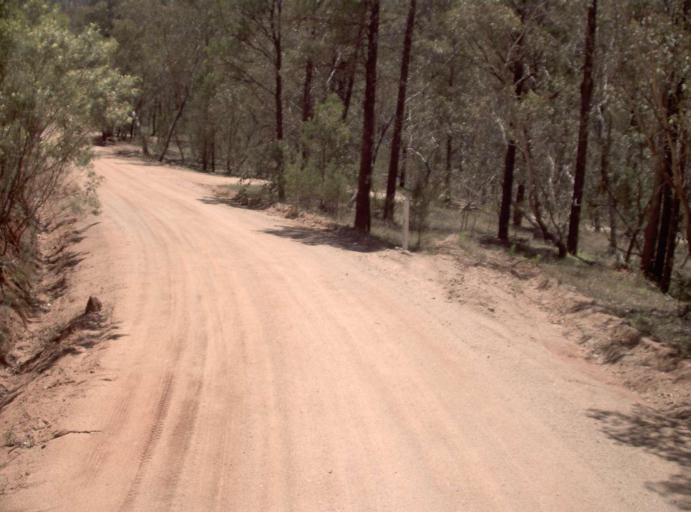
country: AU
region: New South Wales
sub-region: Snowy River
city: Jindabyne
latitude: -36.8951
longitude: 148.4224
